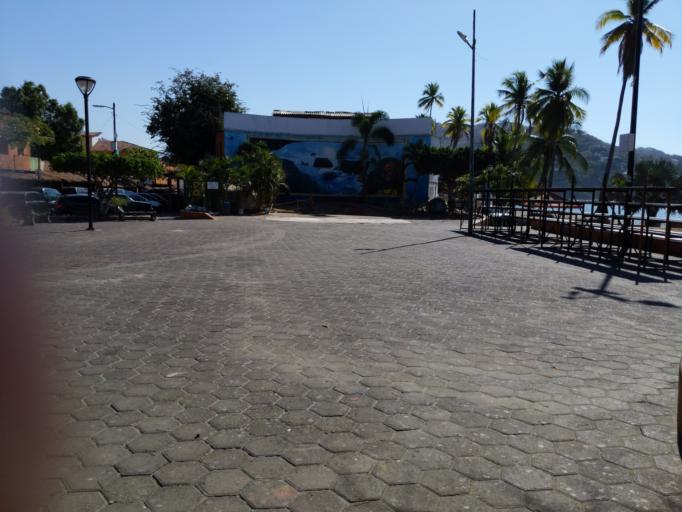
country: MX
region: Guerrero
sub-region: Zihuatanejo de Azueta
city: Ixtapa-Zihuatanejo
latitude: 17.6383
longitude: -101.5580
